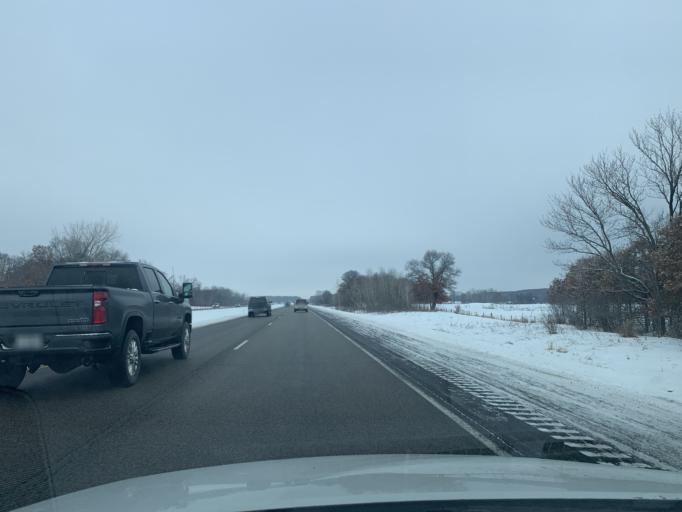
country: US
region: Minnesota
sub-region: Chisago County
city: Stacy
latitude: 45.4207
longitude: -92.9896
